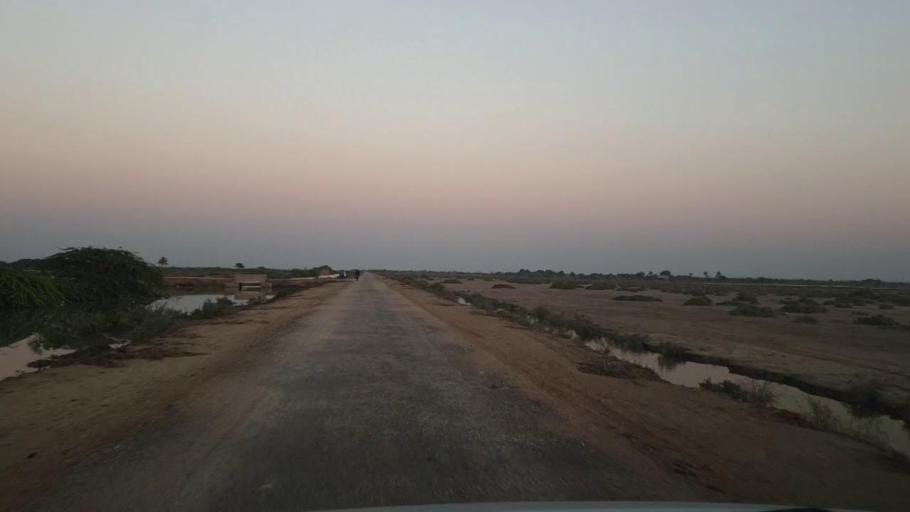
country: PK
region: Sindh
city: Mirpur Sakro
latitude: 24.3856
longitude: 67.5732
